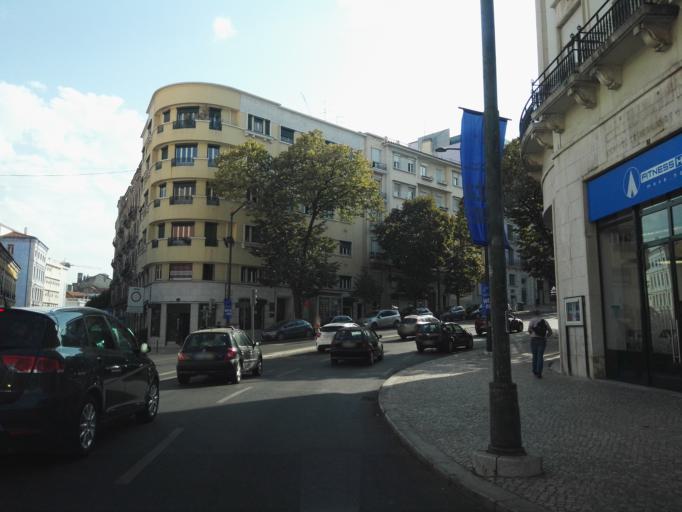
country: PT
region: Lisbon
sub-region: Lisbon
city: Lisbon
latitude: 38.7247
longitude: -9.1462
